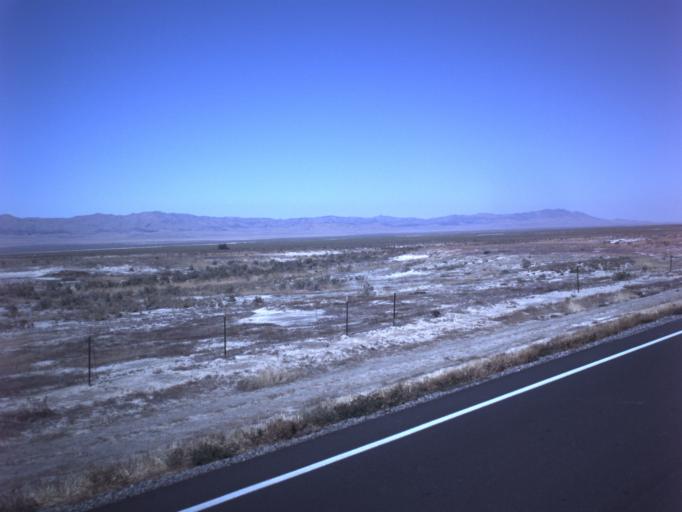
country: US
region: Utah
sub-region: Tooele County
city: Grantsville
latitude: 40.4523
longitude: -112.7481
